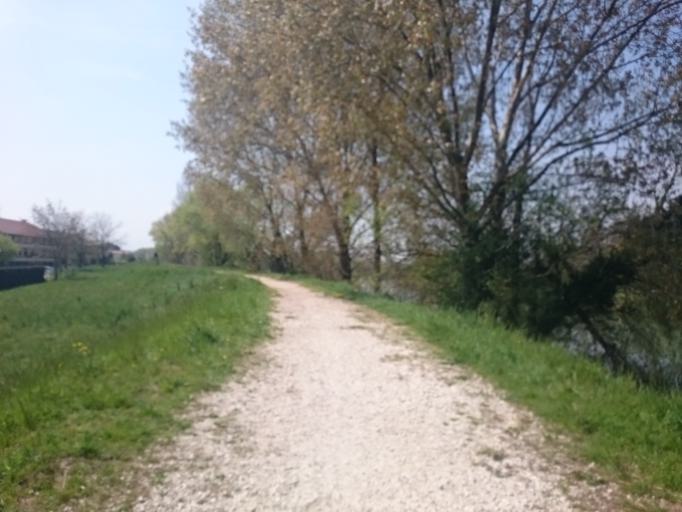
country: IT
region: Veneto
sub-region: Provincia di Padova
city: Mandriola-Sant'Agostino
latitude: 45.3917
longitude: 11.8375
